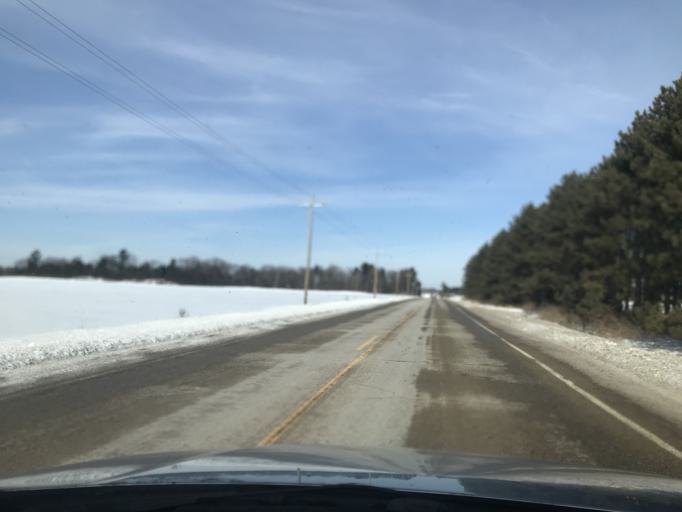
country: US
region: Wisconsin
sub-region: Oconto County
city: Oconto Falls
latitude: 45.1172
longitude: -88.1782
